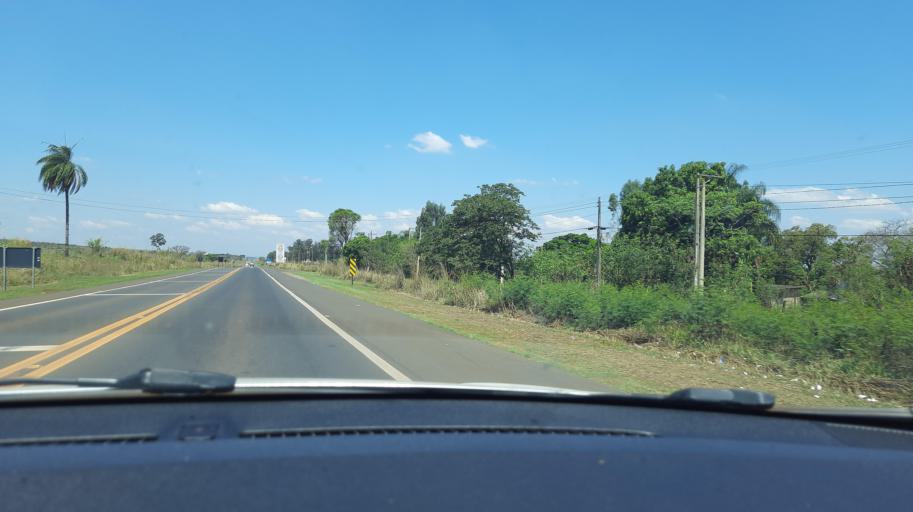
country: BR
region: Sao Paulo
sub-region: Casa Branca
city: Casa Branca
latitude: -21.7762
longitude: -47.0588
